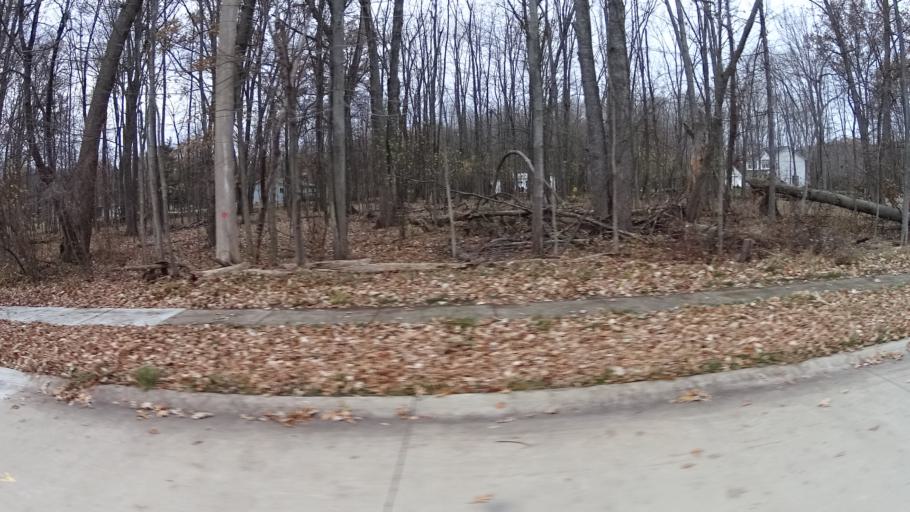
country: US
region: Ohio
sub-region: Lorain County
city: North Ridgeville
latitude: 41.3875
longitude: -82.0638
